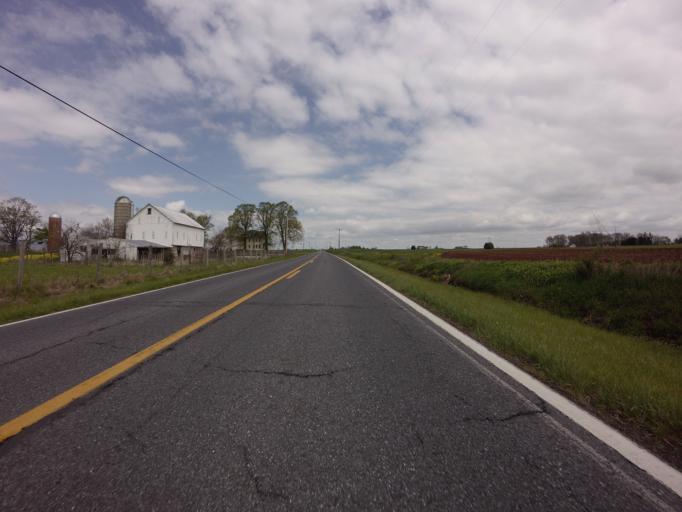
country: US
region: Maryland
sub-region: Frederick County
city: Thurmont
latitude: 39.5936
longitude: -77.3590
